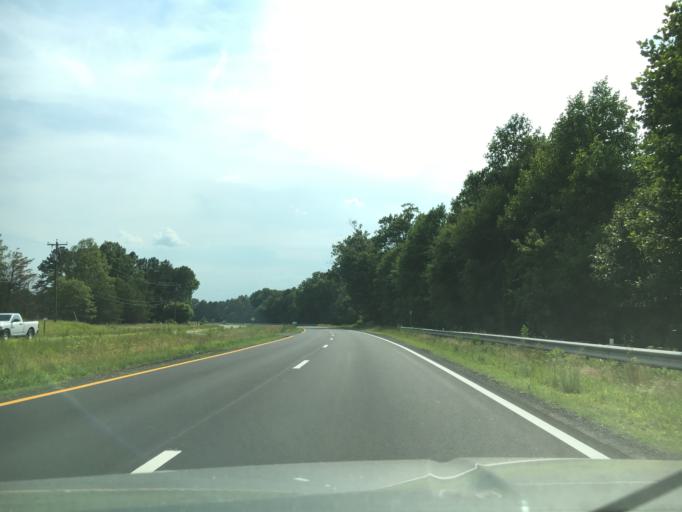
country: US
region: Virginia
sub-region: Halifax County
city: Halifax
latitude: 36.8146
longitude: -78.7481
